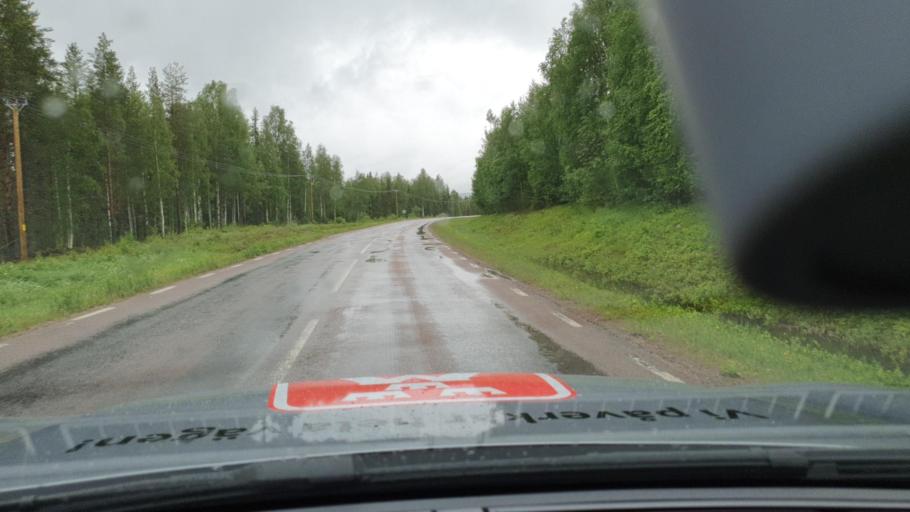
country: SE
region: Norrbotten
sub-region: Overkalix Kommun
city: OEverkalix
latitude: 66.4433
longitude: 23.2273
